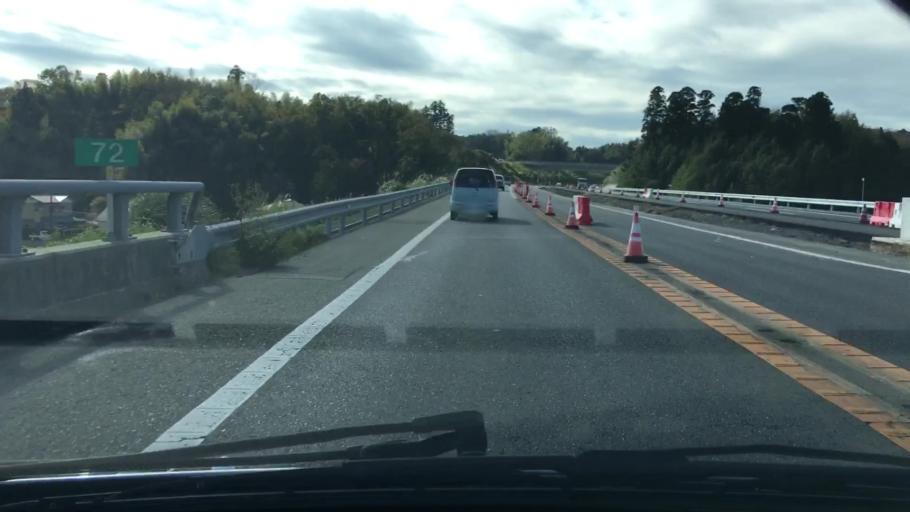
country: JP
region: Chiba
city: Kimitsu
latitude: 35.3047
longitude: 139.9414
